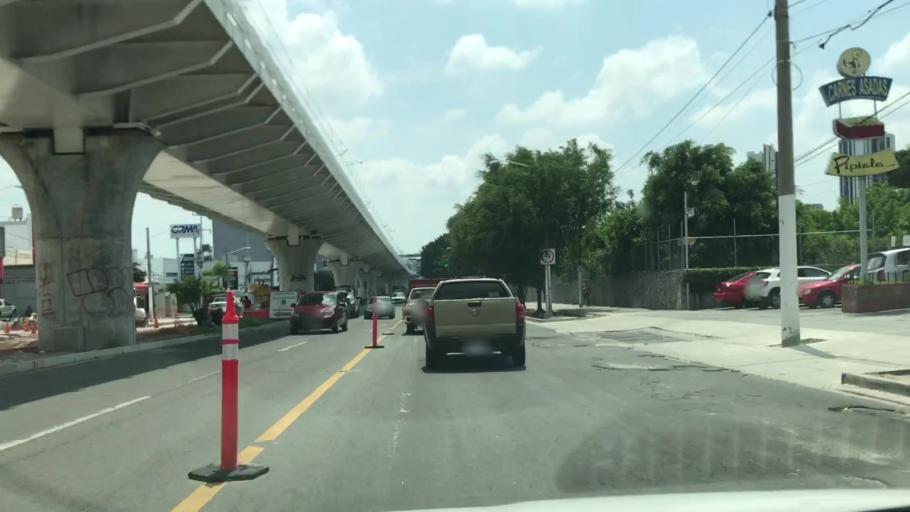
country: MX
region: Jalisco
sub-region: Zapopan
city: Zapopan
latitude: 20.7170
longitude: -103.3826
